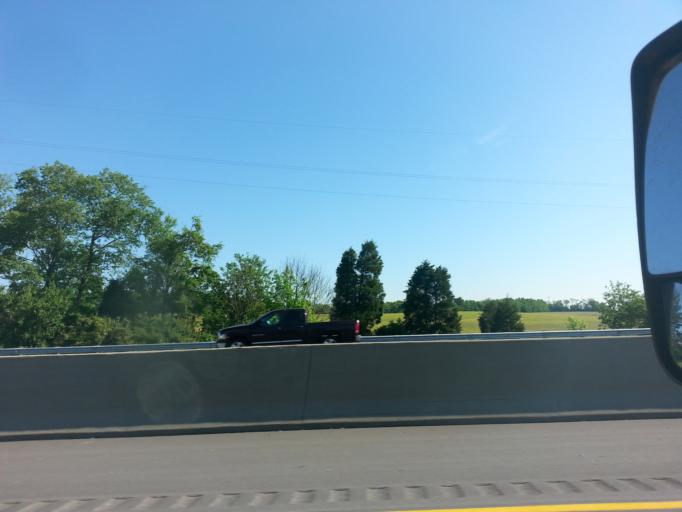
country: US
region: Kentucky
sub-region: Shelby County
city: Simpsonville
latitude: 38.2016
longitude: -85.3097
